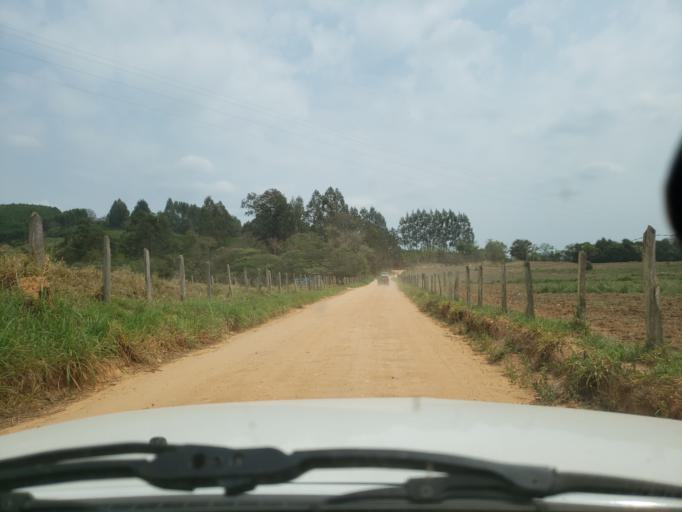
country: BR
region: Minas Gerais
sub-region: Jacutinga
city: Jacutinga
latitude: -22.3182
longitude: -46.5986
